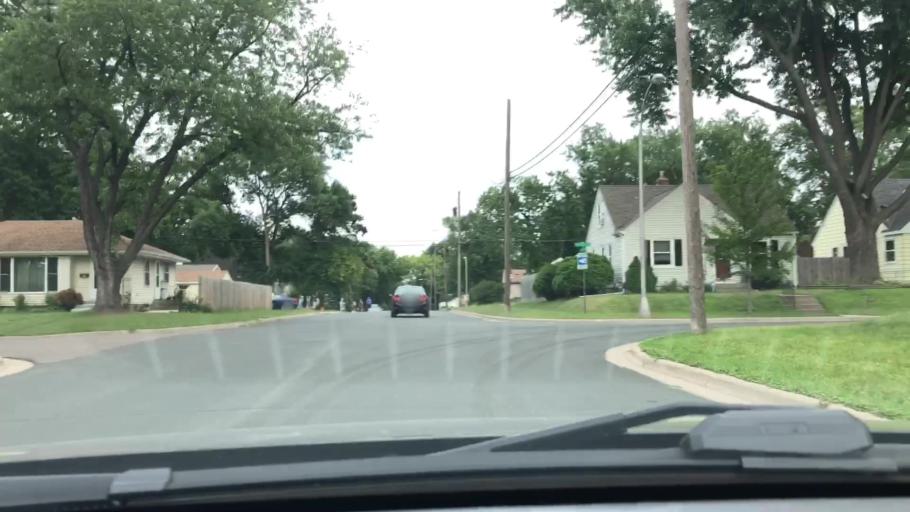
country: US
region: Minnesota
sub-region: Hennepin County
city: Richfield
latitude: 44.8727
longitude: -93.2772
